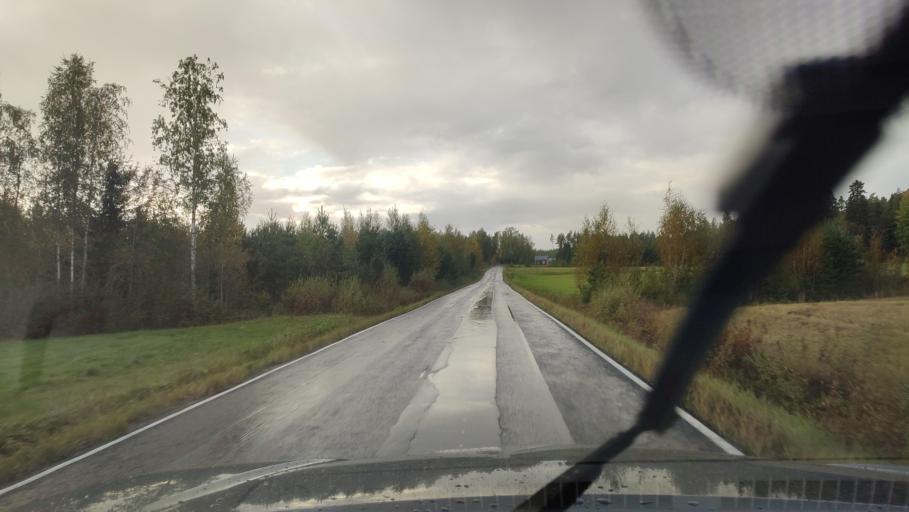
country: FI
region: Southern Ostrobothnia
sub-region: Suupohja
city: Karijoki
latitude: 62.3156
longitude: 21.6912
